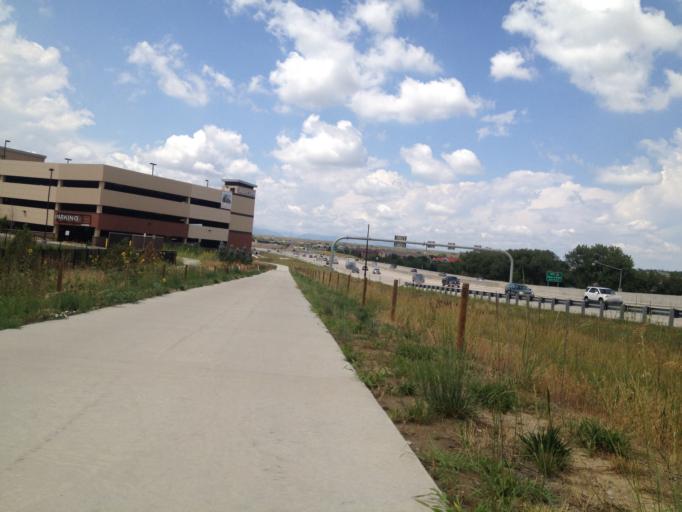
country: US
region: Colorado
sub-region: Boulder County
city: Superior
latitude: 39.9528
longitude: -105.1577
